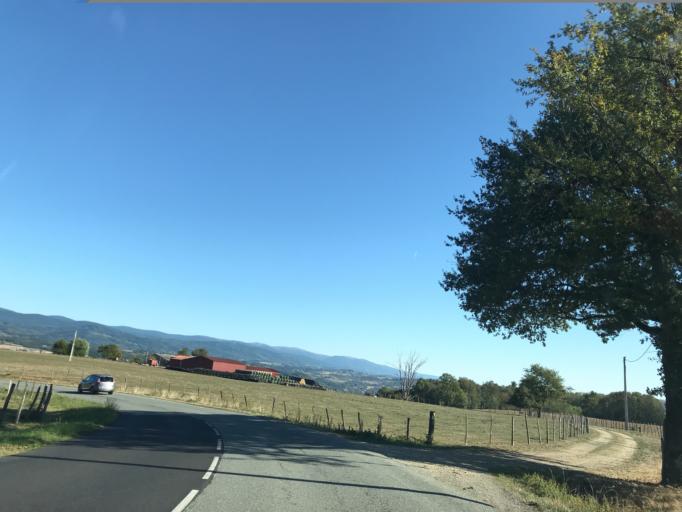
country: FR
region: Auvergne
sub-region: Departement du Puy-de-Dome
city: Courpiere
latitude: 45.7681
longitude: 3.5140
